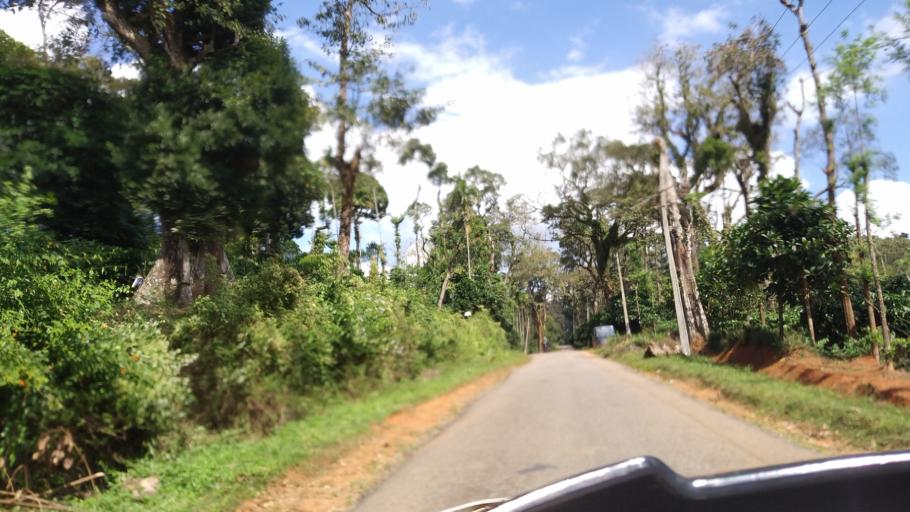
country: IN
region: Karnataka
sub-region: Kodagu
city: Ponnampet
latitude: 12.0341
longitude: 75.9025
